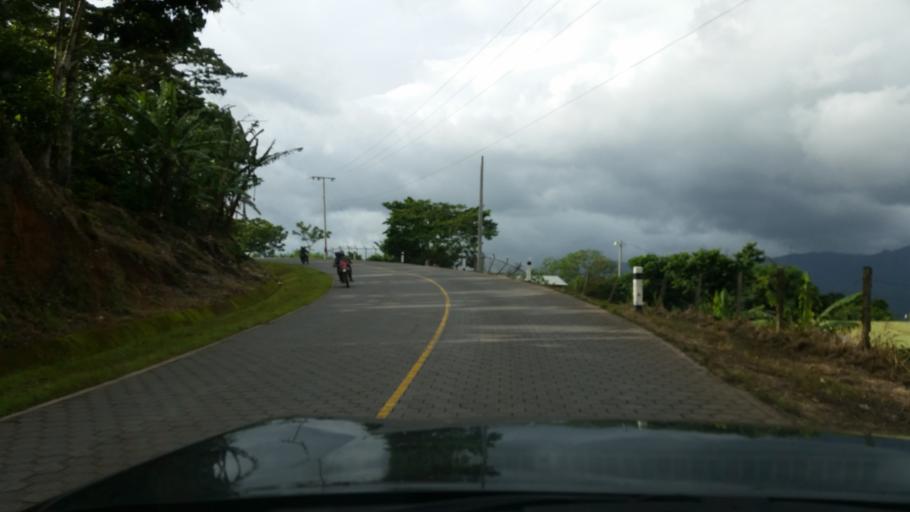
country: NI
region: Matagalpa
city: San Ramon
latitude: 13.1746
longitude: -85.7297
